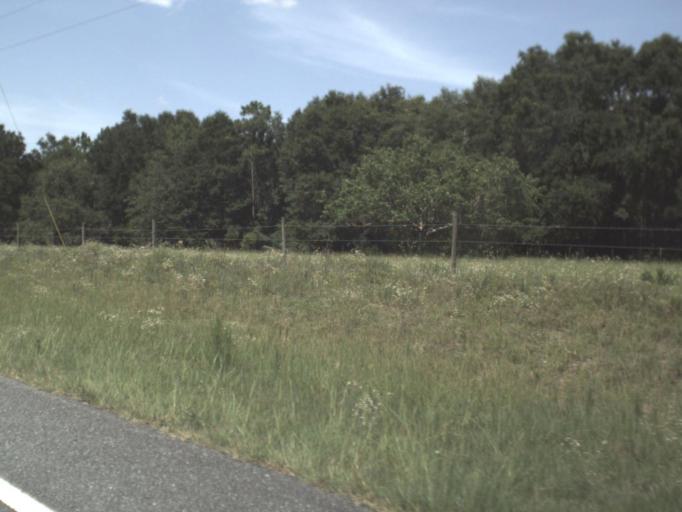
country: US
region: Florida
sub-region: Gilchrist County
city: Trenton
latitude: 29.7369
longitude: -82.7415
